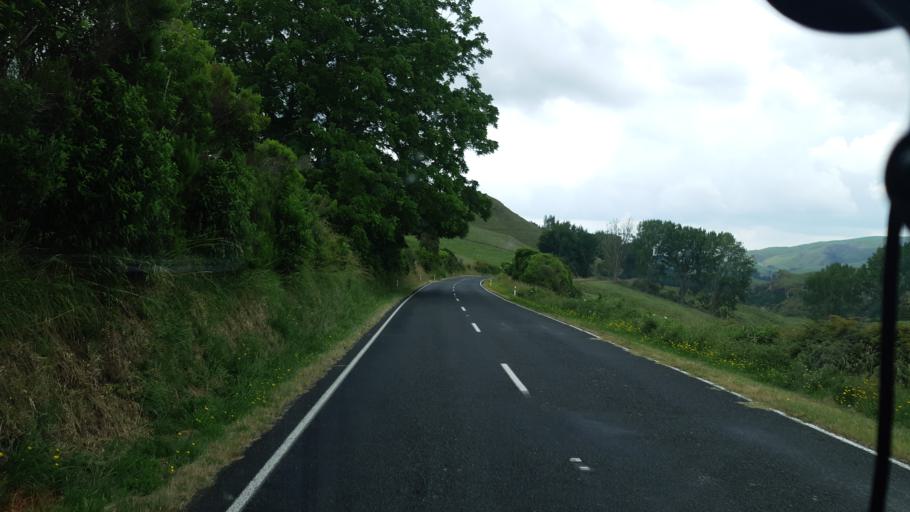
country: NZ
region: Waikato
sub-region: Waipa District
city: Cambridge
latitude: -38.1322
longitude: 175.5193
